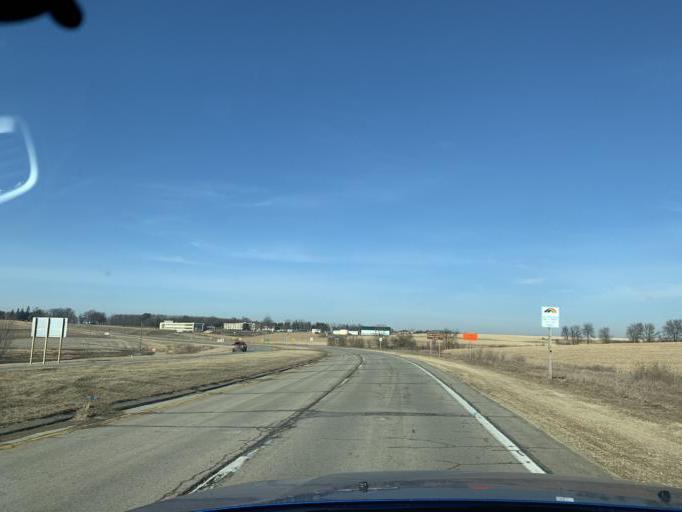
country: US
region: Wisconsin
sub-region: Green County
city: Monroe
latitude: 42.6154
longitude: -89.6528
